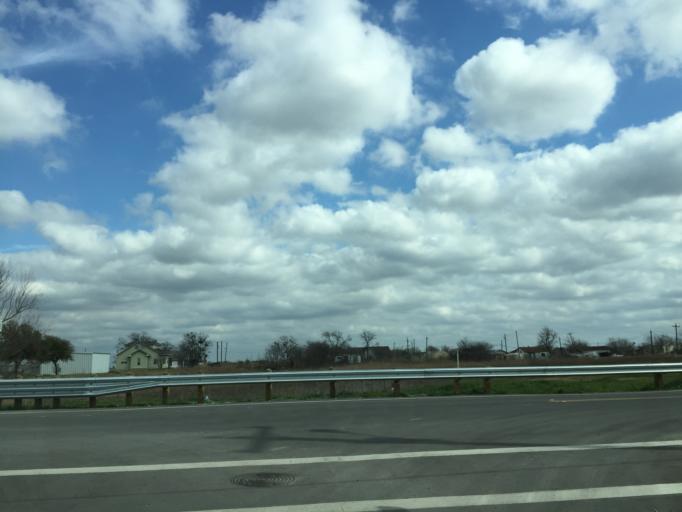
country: US
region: Texas
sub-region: Williamson County
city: Granger
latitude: 30.7183
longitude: -97.4373
